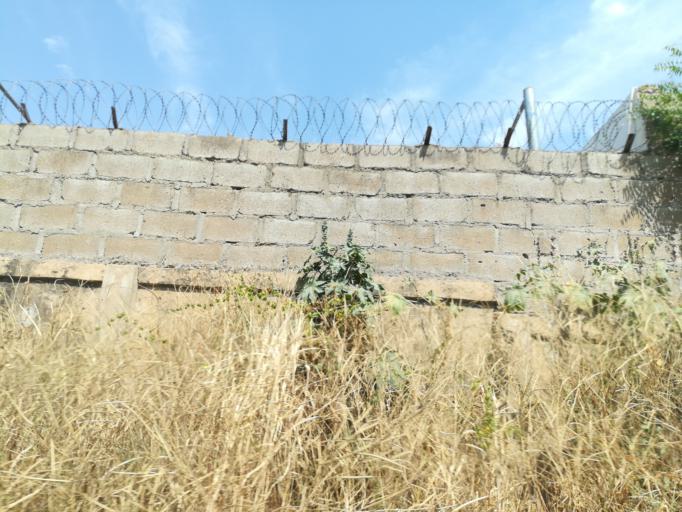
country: NG
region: Kano
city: Kano
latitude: 12.0284
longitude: 8.5218
